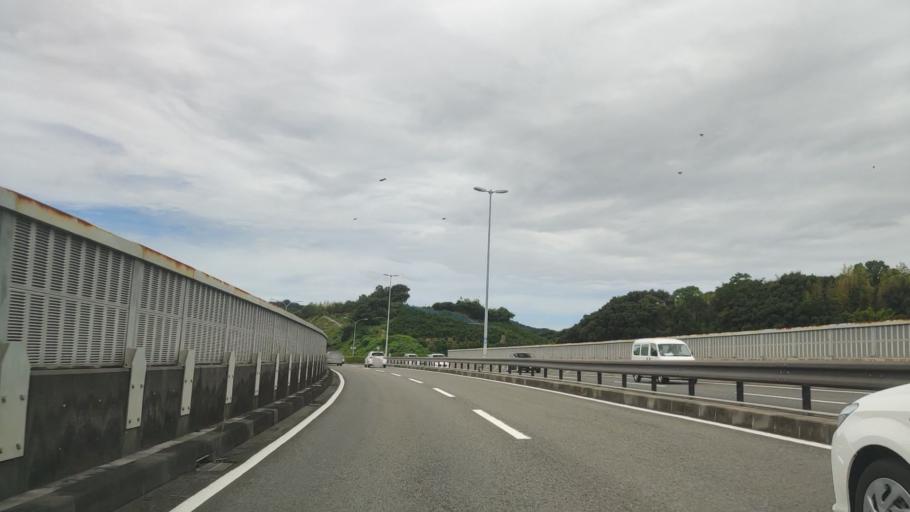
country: JP
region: Wakayama
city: Tanabe
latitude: 33.7438
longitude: 135.3852
